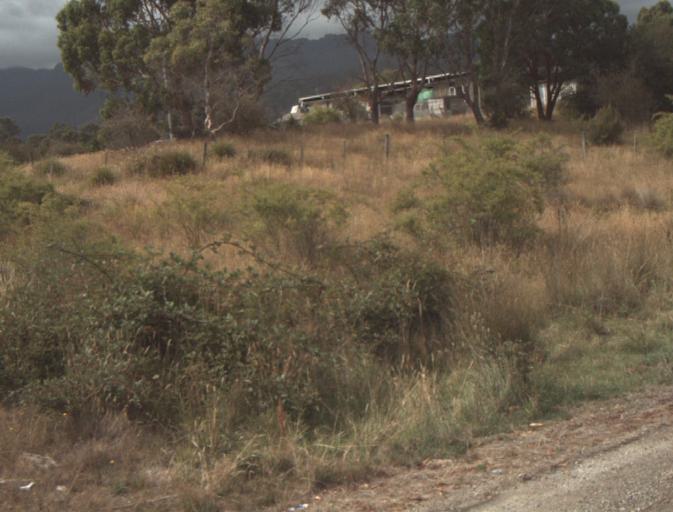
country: AU
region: Tasmania
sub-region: Dorset
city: Scottsdale
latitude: -41.4692
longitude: 147.5731
